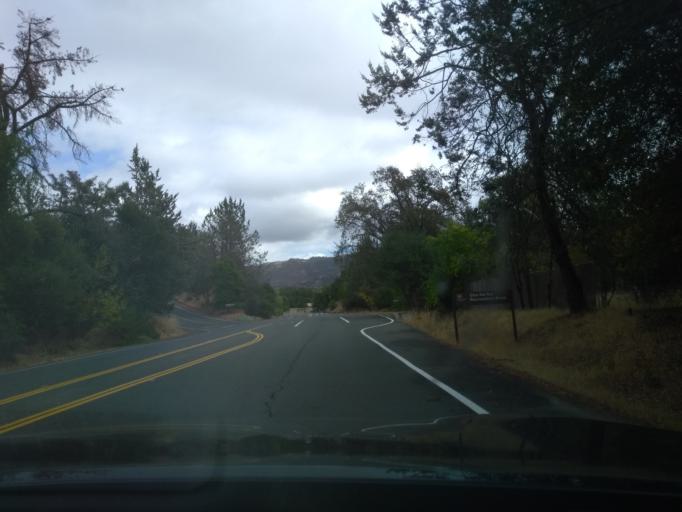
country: US
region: California
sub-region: Mendocino County
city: Ukiah
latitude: 39.2030
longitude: -123.1874
